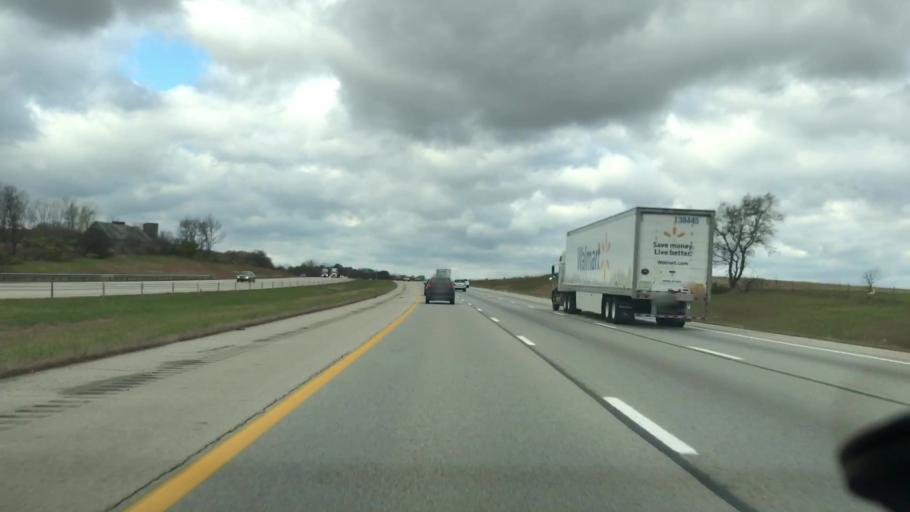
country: US
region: Ohio
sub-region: Clark County
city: Lisbon
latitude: 39.9357
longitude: -83.6636
